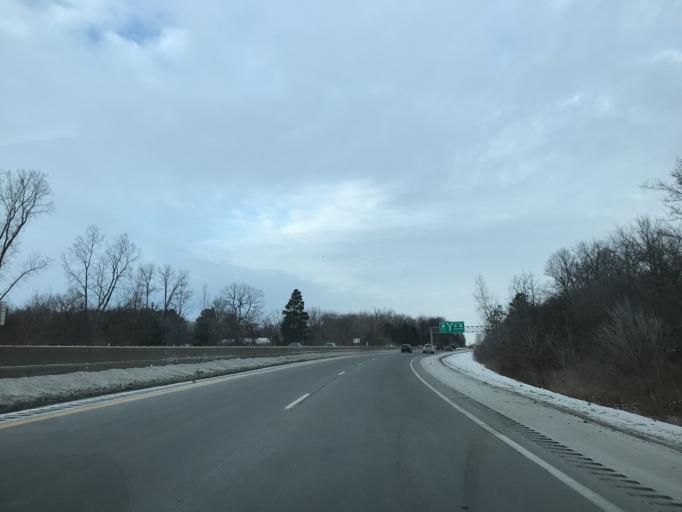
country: US
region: Michigan
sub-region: Washtenaw County
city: Ann Arbor
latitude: 42.3088
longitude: -83.7435
